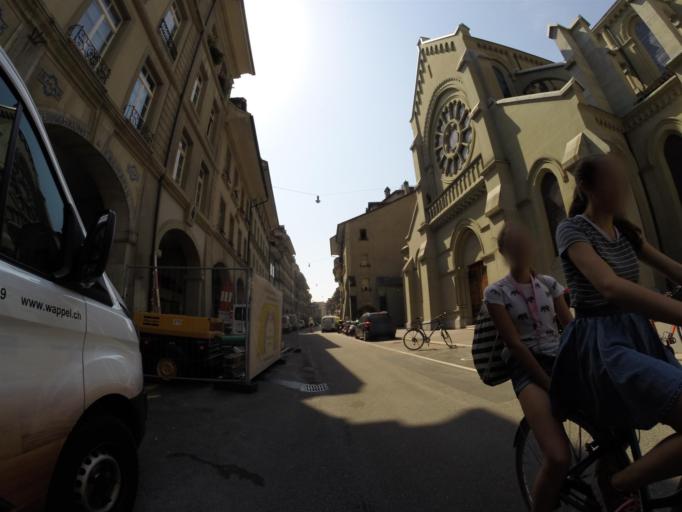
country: CH
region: Bern
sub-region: Bern-Mittelland District
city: Bern
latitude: 46.9485
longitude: 7.4519
